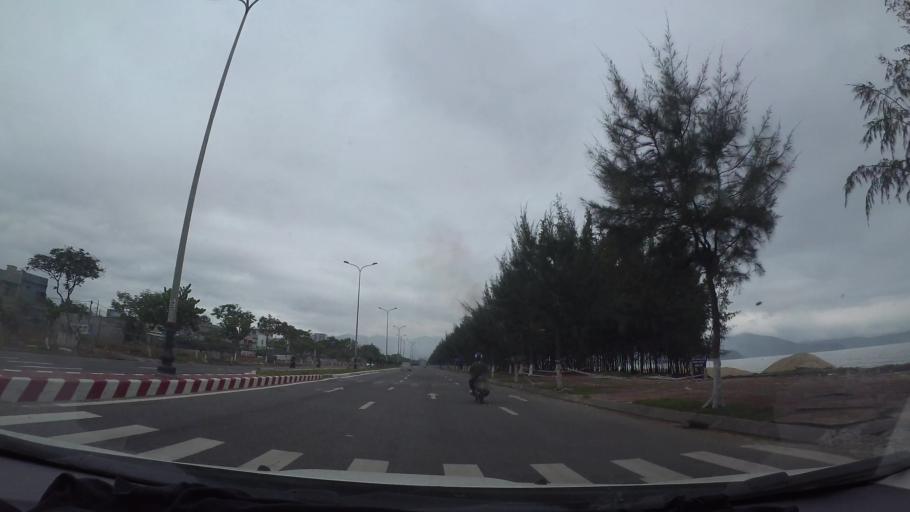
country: VN
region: Da Nang
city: Lien Chieu
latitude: 16.1039
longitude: 108.1377
